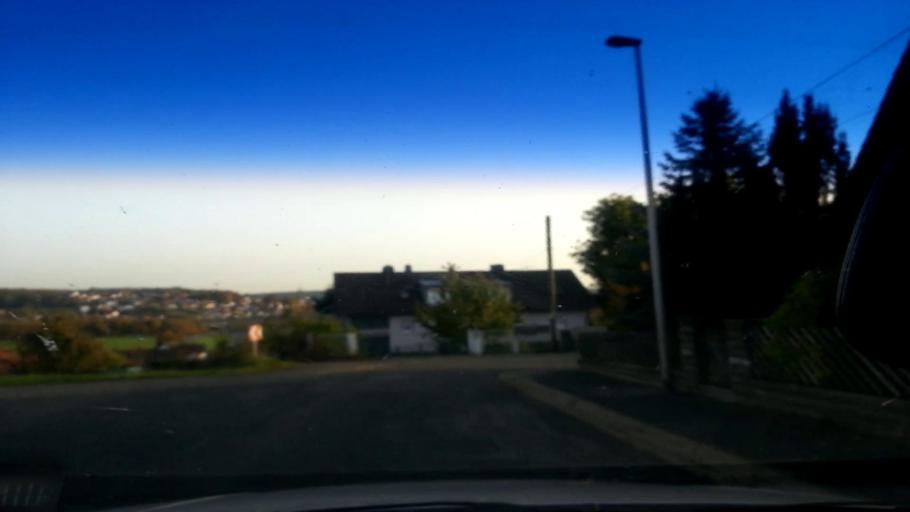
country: DE
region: Bavaria
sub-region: Upper Franconia
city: Memmelsdorf
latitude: 49.9419
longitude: 10.9512
